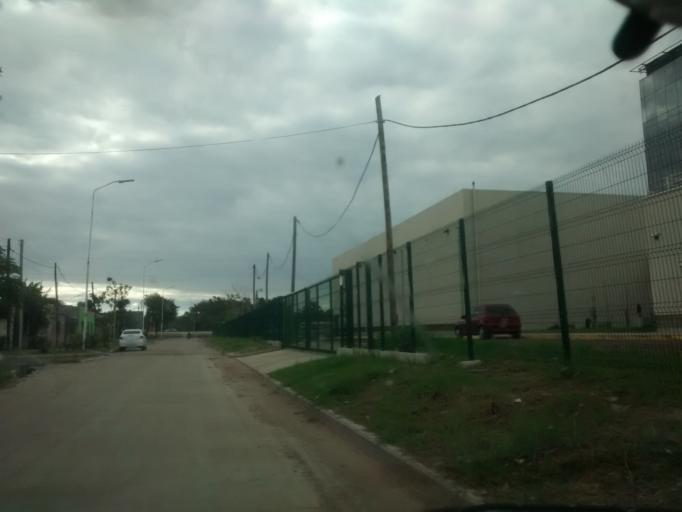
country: AR
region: Chaco
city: Fontana
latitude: -27.4479
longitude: -59.0226
